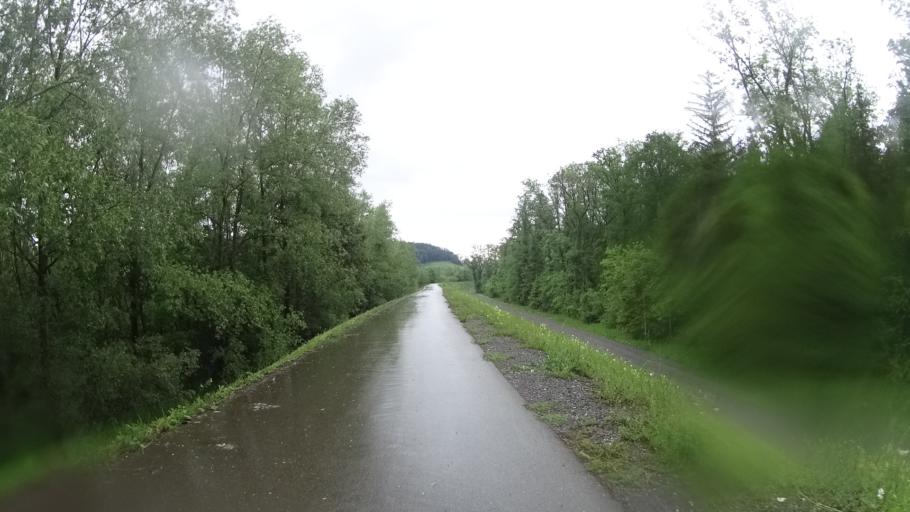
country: CH
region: Saint Gallen
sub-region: Wahlkreis Rheintal
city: Ruthi
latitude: 47.2955
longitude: 9.5586
